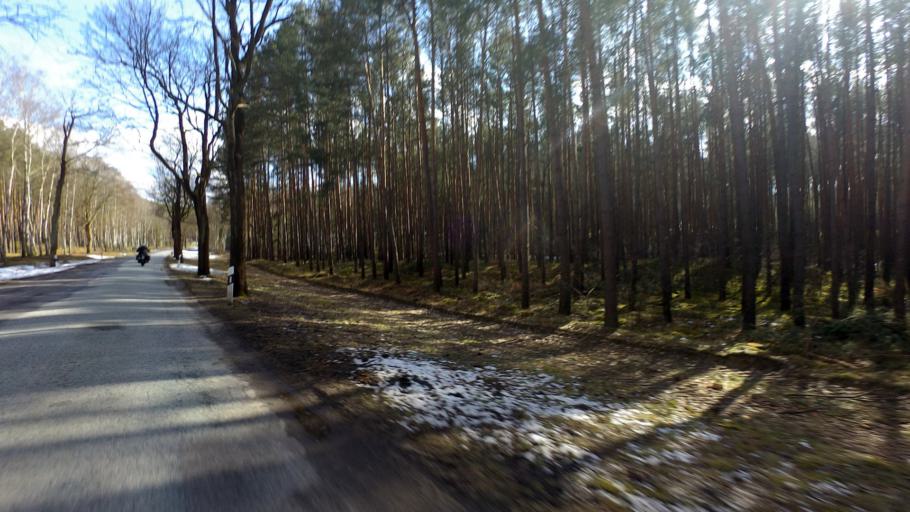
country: DE
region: Brandenburg
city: Marienwerder
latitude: 52.7928
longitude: 13.6023
